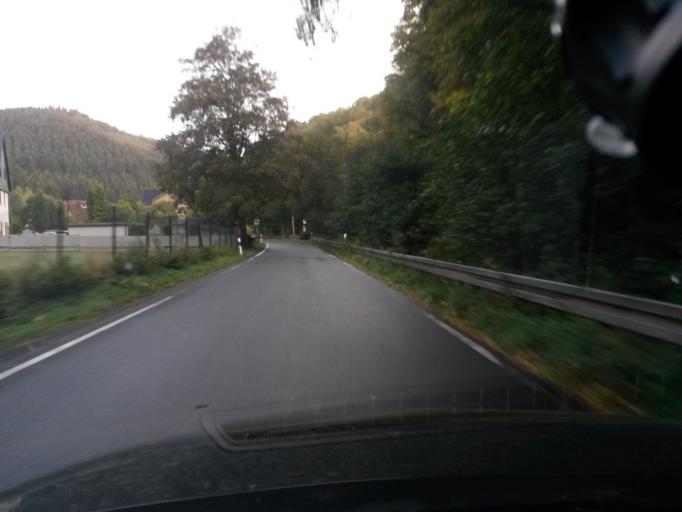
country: DE
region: North Rhine-Westphalia
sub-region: Regierungsbezirk Arnsberg
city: Herscheid
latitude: 51.2180
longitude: 7.7249
